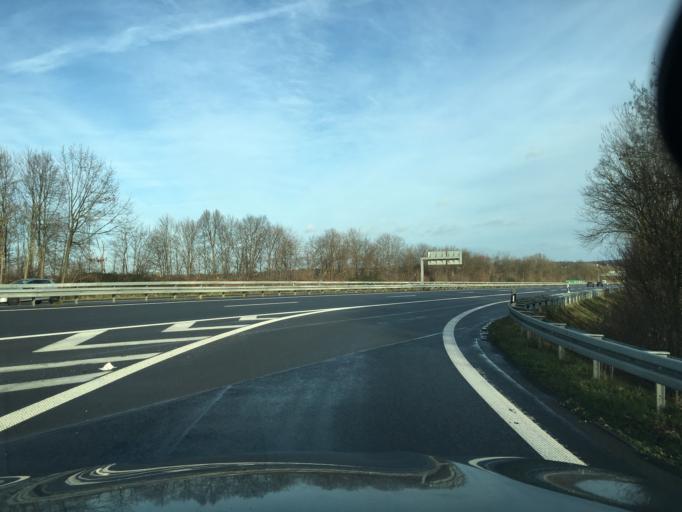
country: DE
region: North Rhine-Westphalia
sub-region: Regierungsbezirk Koln
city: Weilerswist
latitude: 50.7712
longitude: 6.8261
